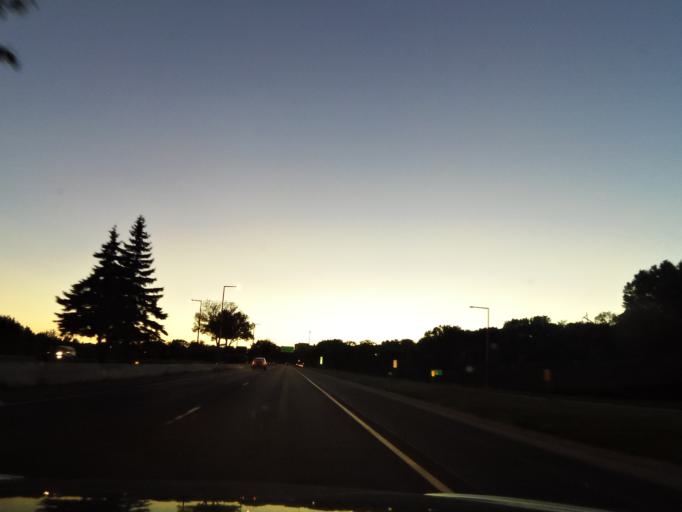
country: US
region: Minnesota
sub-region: Dakota County
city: West Saint Paul
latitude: 44.9315
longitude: -93.1333
